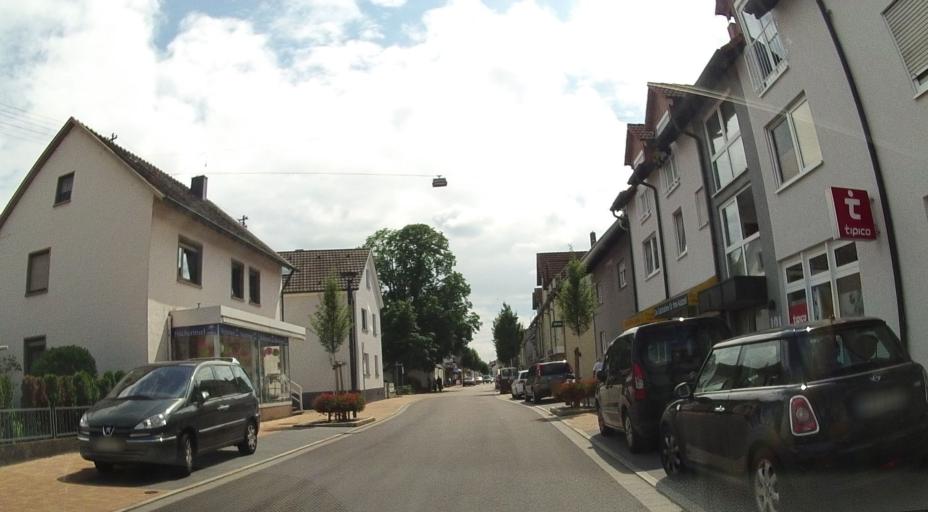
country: DE
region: Baden-Wuerttemberg
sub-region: Karlsruhe Region
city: Durmersheim
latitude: 48.9360
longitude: 8.2714
